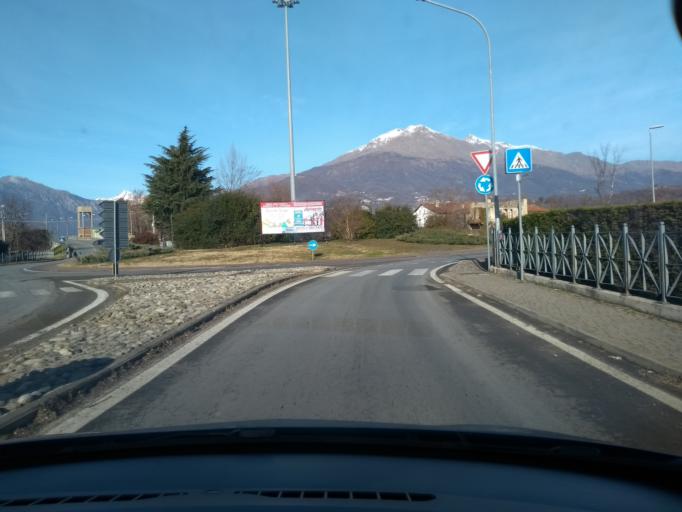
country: IT
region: Piedmont
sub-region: Provincia di Torino
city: Valperga
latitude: 45.3832
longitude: 7.6637
